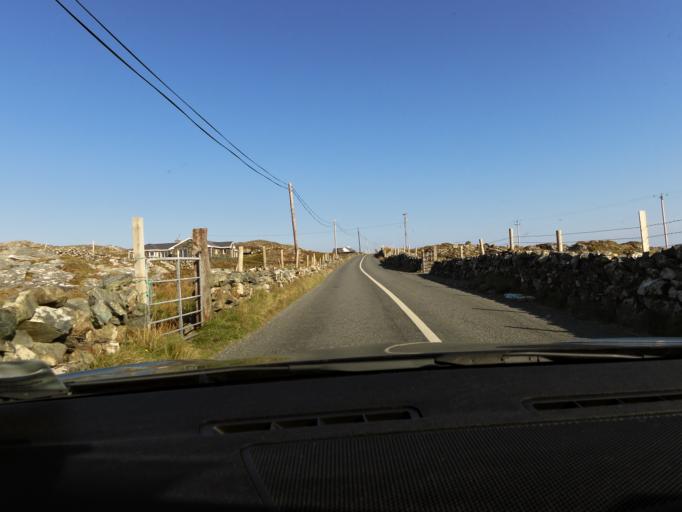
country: IE
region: Connaught
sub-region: County Galway
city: Clifden
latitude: 53.3960
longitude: -10.0218
